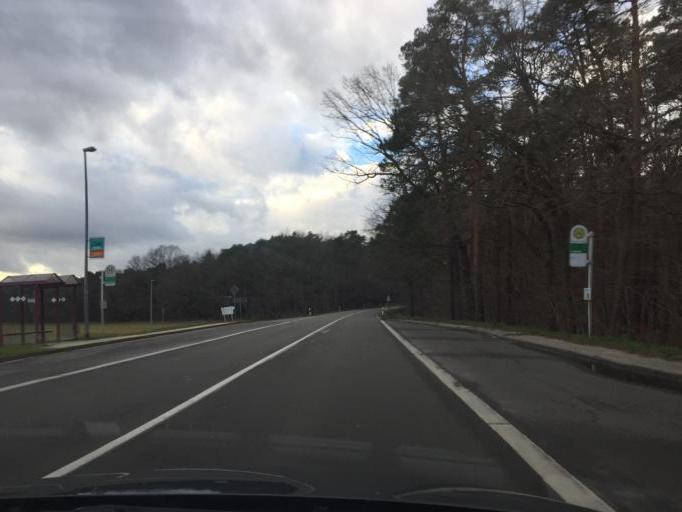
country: DE
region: Brandenburg
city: Kolkwitz
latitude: 51.7509
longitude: 14.2044
